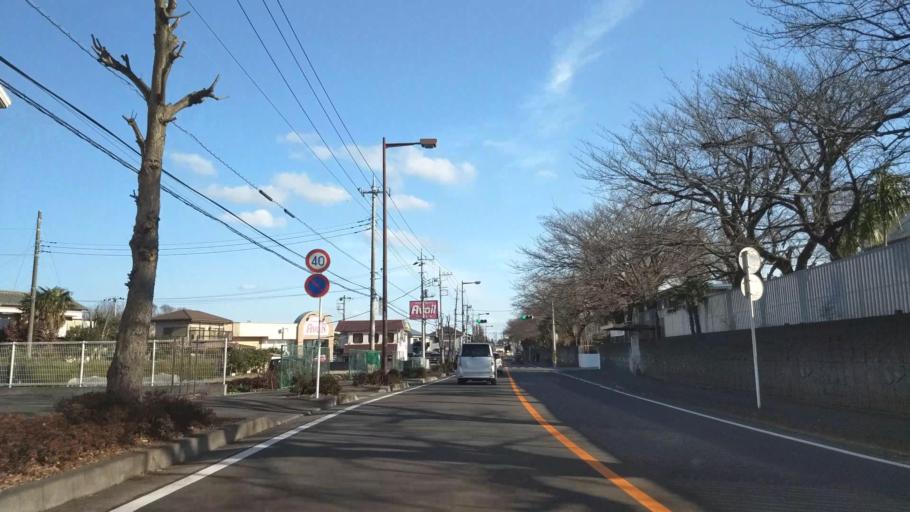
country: JP
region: Kanagawa
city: Hadano
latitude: 35.3633
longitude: 139.2578
